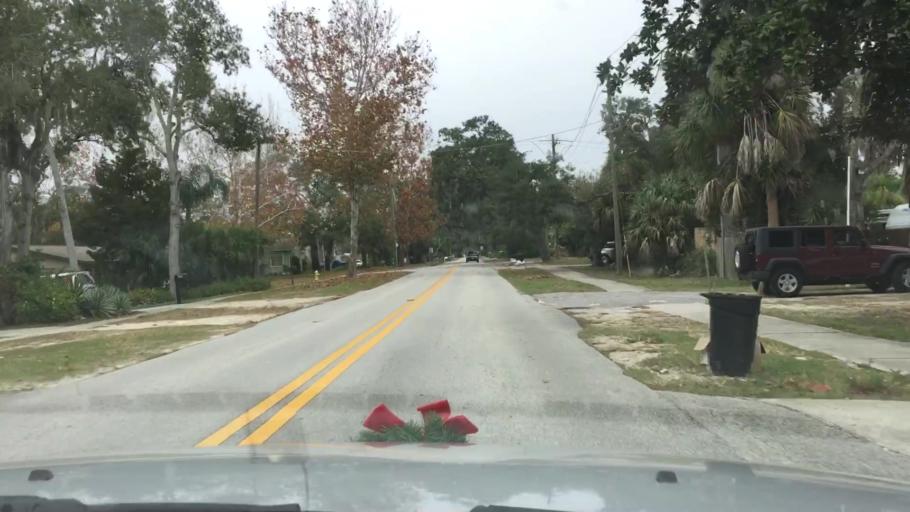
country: US
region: Florida
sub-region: Volusia County
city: Ormond Beach
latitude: 29.2940
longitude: -81.0632
